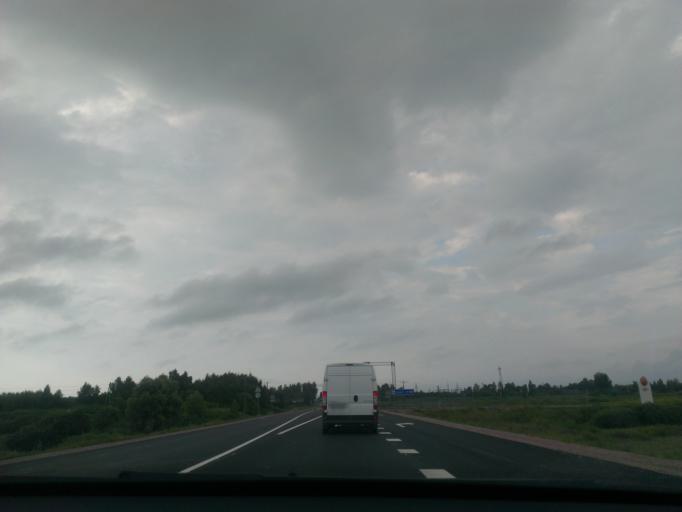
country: LV
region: Lecava
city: Iecava
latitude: 56.6229
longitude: 24.2196
